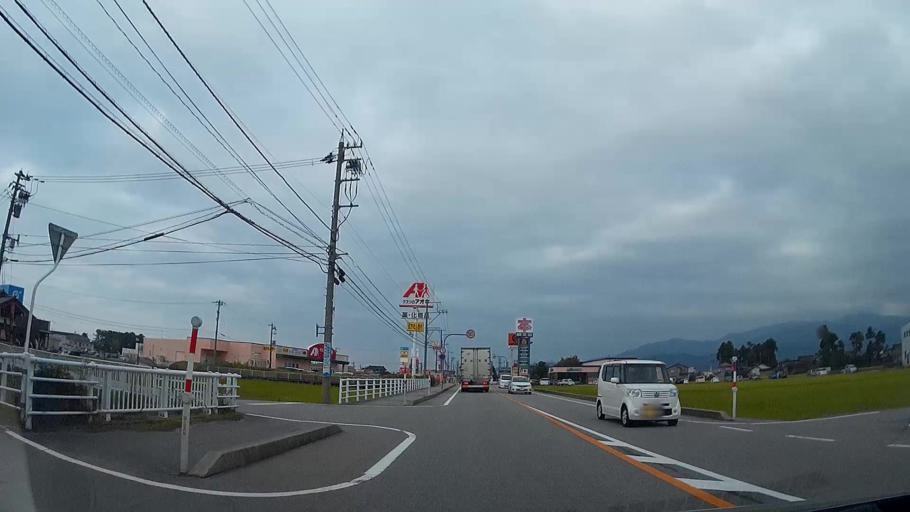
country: JP
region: Toyama
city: Nyuzen
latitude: 36.9393
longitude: 137.5137
